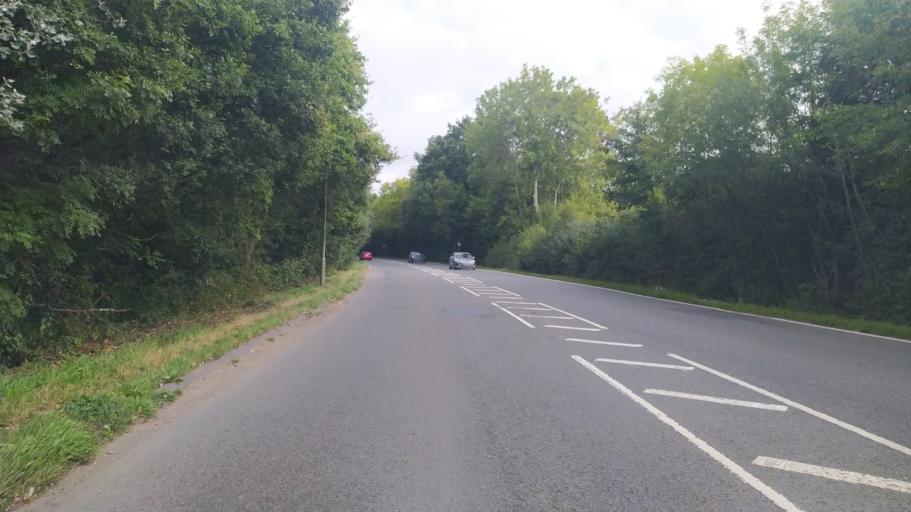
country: GB
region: England
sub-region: Hampshire
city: Totton
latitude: 50.9074
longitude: -1.4871
